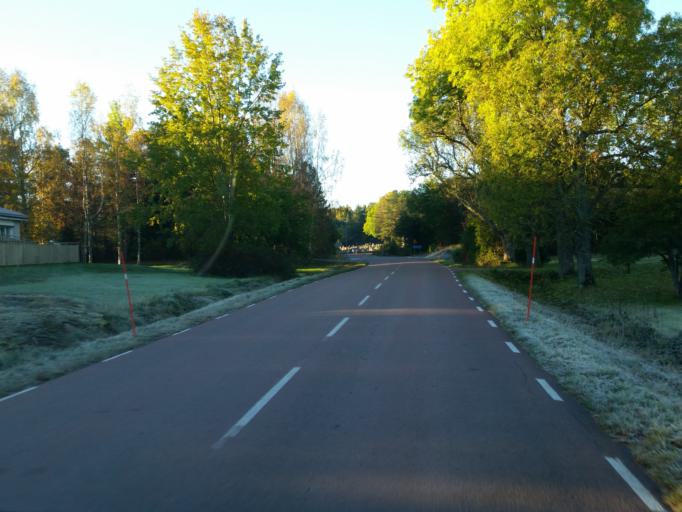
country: AX
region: Alands skaergard
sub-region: Vardoe
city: Vardoe
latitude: 60.2443
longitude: 20.3751
